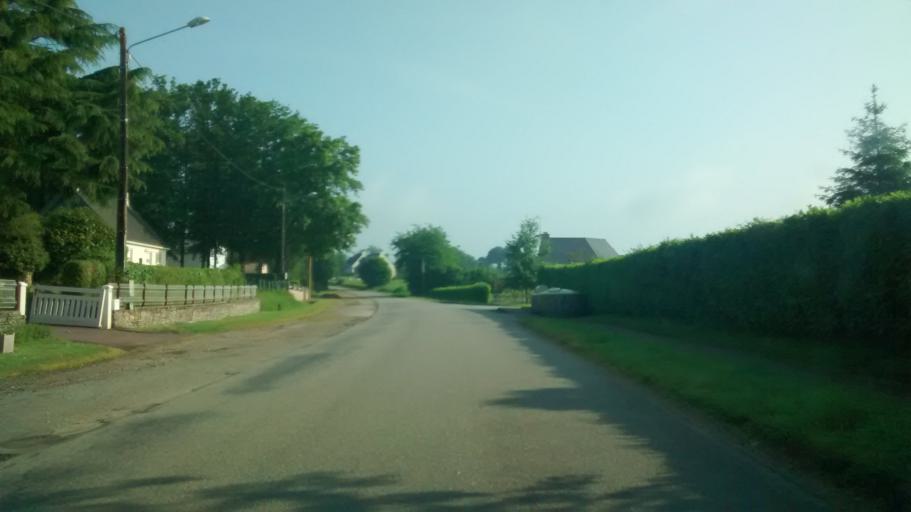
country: FR
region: Brittany
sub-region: Departement du Morbihan
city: Ruffiac
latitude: 47.8214
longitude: -2.2826
